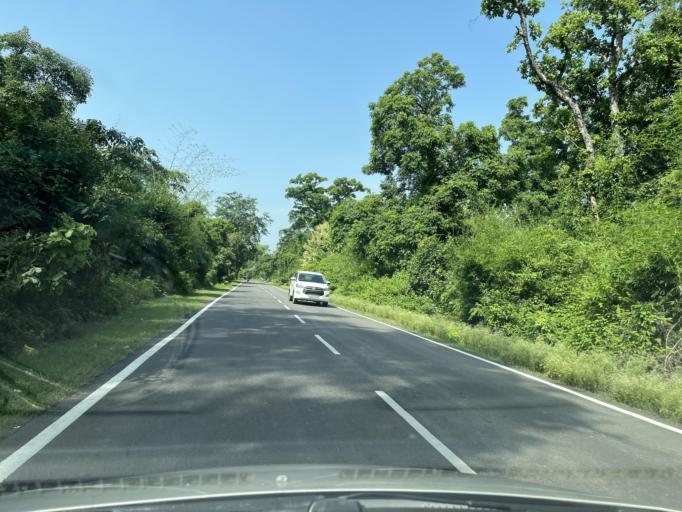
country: IN
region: Uttarakhand
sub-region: Naini Tal
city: Kaladhungi
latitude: 29.2229
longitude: 79.2393
